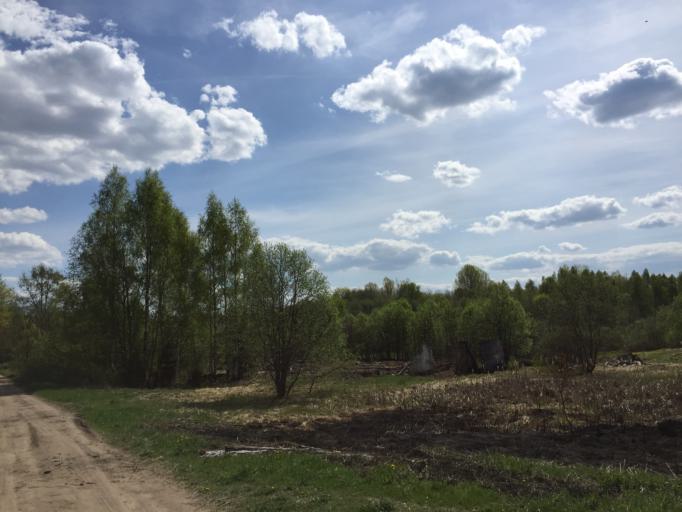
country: LV
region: Limbazu Rajons
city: Limbazi
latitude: 57.3520
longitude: 24.6602
